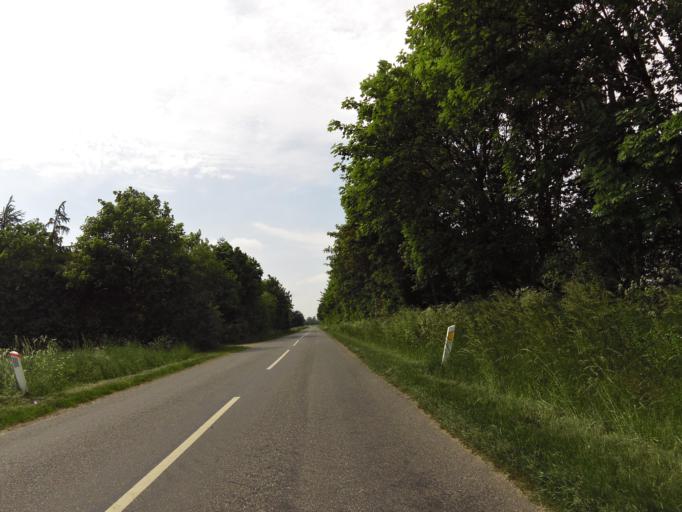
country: DK
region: South Denmark
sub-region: Haderslev Kommune
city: Gram
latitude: 55.2759
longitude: 9.1164
